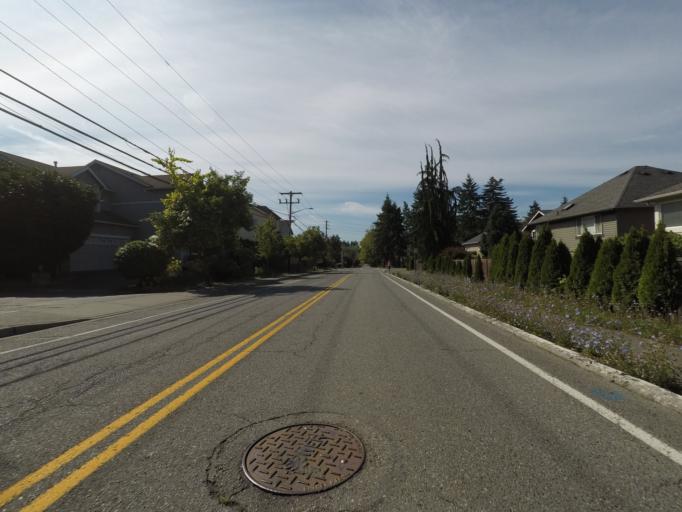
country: US
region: Washington
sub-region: King County
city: Inglewood-Finn Hill
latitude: 47.7125
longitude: -122.2296
